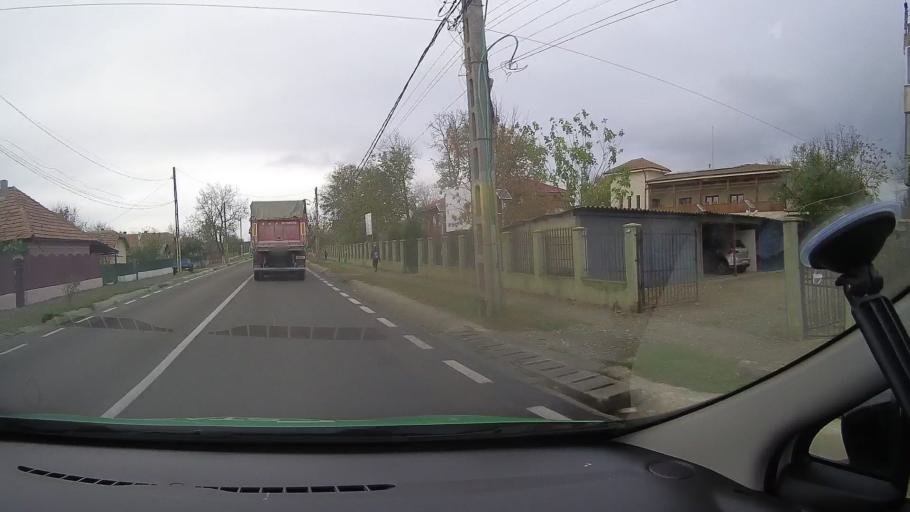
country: RO
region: Constanta
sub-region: Comuna Poarta Alba
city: Poarta Alba
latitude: 44.2087
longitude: 28.3947
